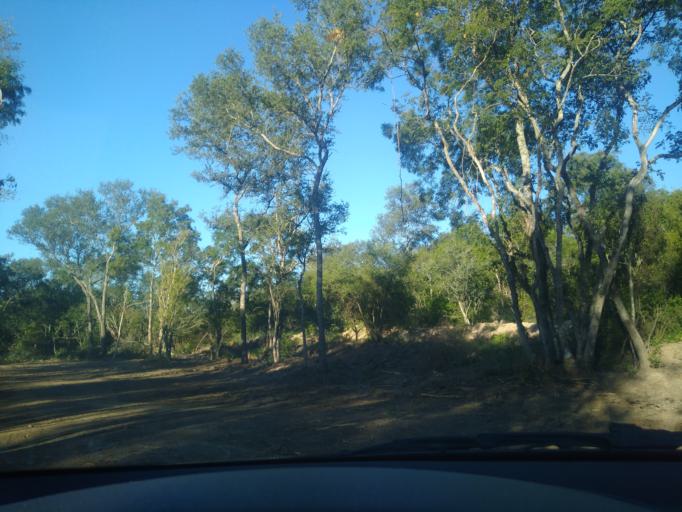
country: AR
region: Chaco
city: Resistencia
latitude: -27.4150
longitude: -58.9539
